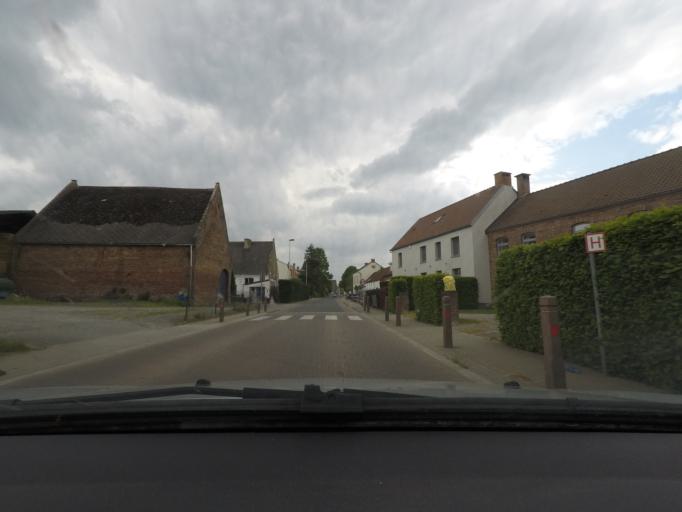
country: BE
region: Wallonia
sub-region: Province du Hainaut
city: Basse Lasne
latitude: 50.6605
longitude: 4.5206
